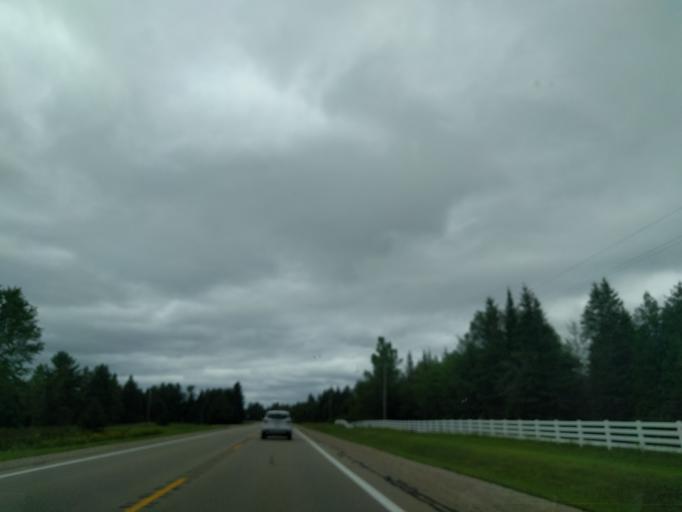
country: US
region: Michigan
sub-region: Delta County
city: Escanaba
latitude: 45.5244
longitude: -87.2881
